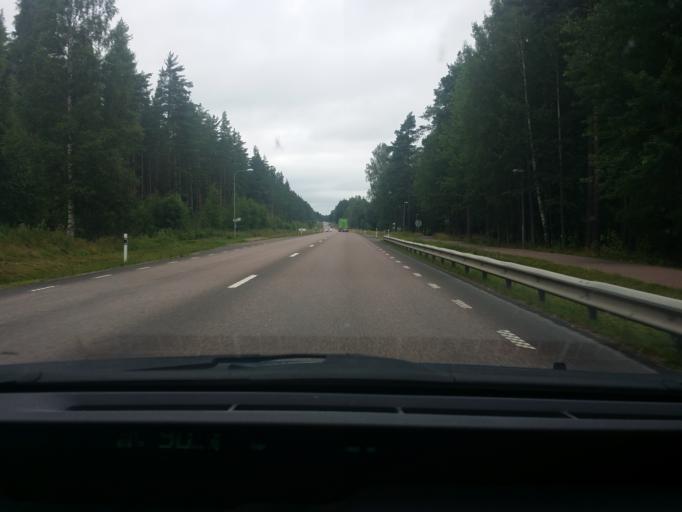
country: SE
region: Dalarna
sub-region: Borlange Kommun
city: Borlaenge
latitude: 60.5187
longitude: 15.3677
